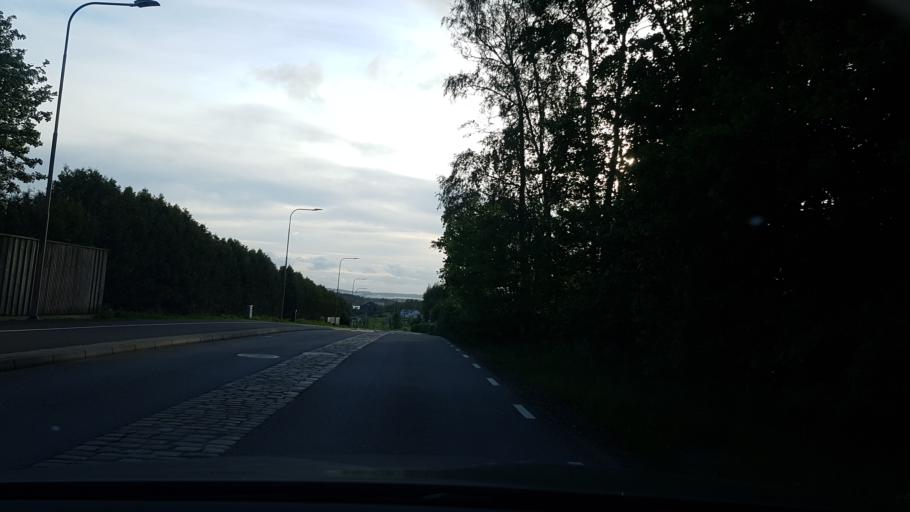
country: SE
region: Vaestra Goetaland
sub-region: Goteborg
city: Billdal
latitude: 57.5997
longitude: 11.9397
